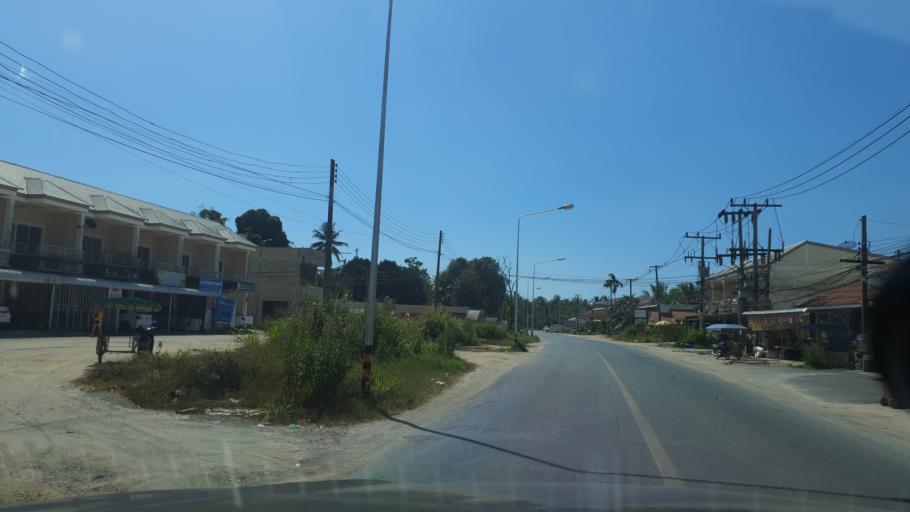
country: TH
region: Phangnga
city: Ban Khao Lak
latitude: 8.5914
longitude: 98.2548
